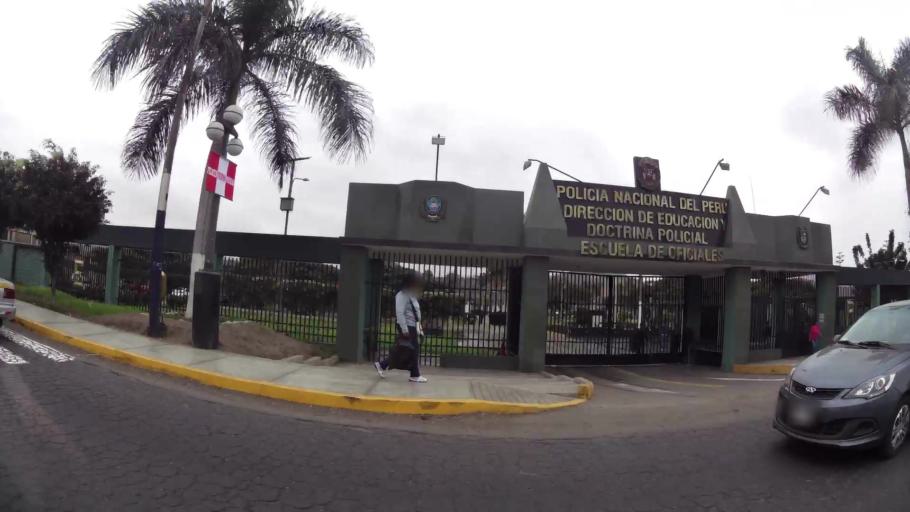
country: PE
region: Lima
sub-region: Lima
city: Surco
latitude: -12.1753
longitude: -76.9938
